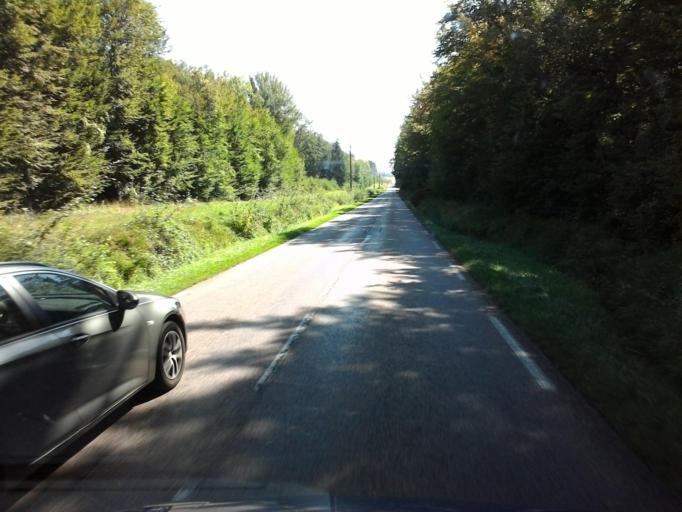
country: FR
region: Bourgogne
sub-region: Departement de l'Yonne
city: Joux-la-Ville
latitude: 47.5873
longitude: 3.8702
